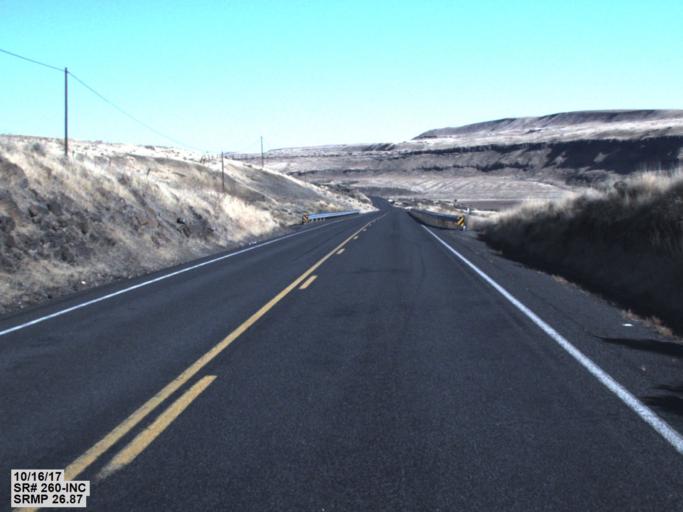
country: US
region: Washington
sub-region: Franklin County
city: Connell
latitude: 46.6504
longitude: -118.5150
